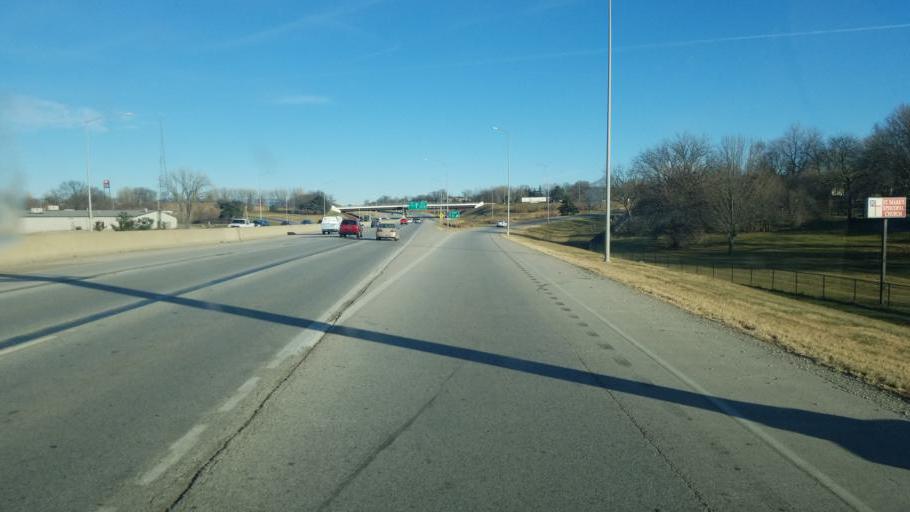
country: US
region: Iowa
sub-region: Polk County
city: Des Moines
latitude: 41.6235
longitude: -93.5756
